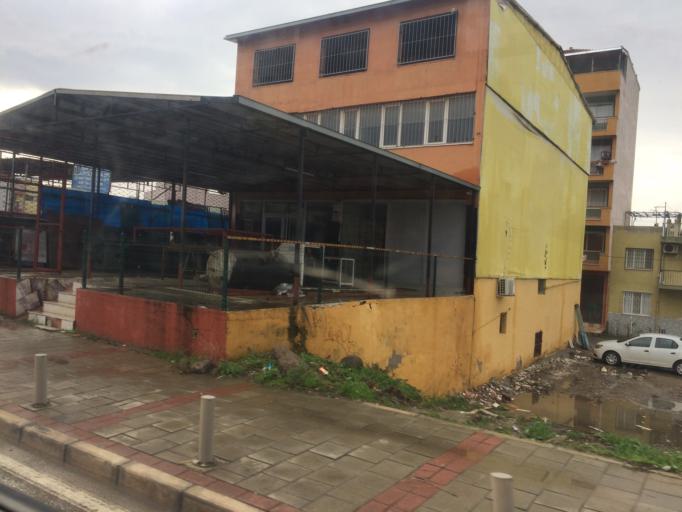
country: TR
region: Izmir
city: Karsiyaka
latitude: 38.5180
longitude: 27.0406
